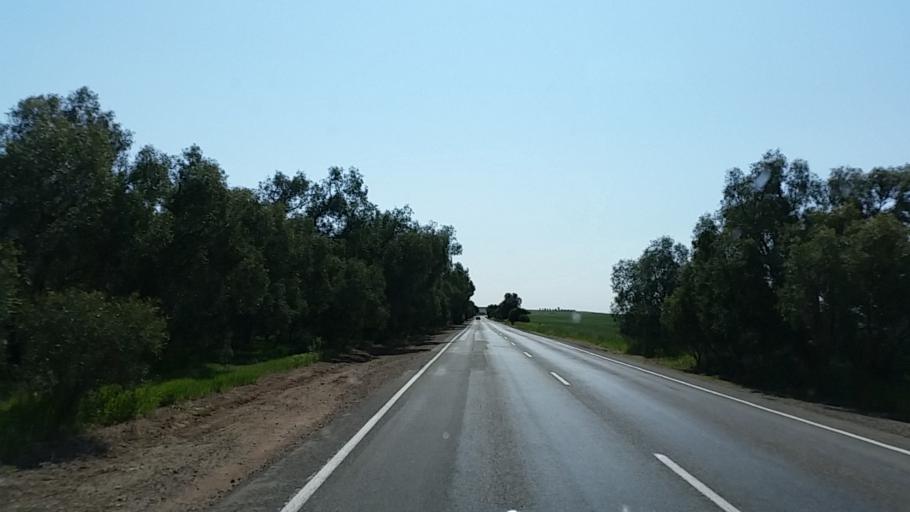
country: AU
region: South Australia
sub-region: Northern Areas
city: Jamestown
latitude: -33.2207
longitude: 138.4116
